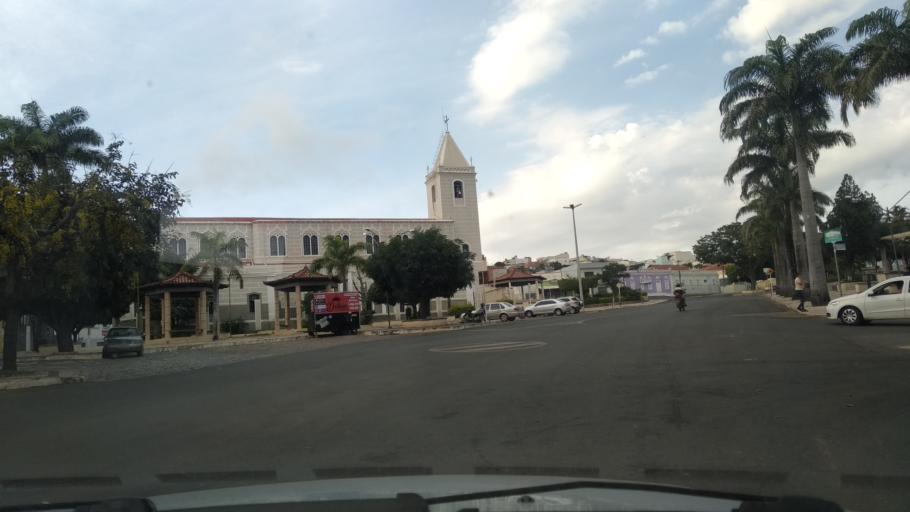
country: BR
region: Bahia
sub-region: Caetite
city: Caetite
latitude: -14.0684
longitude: -42.4848
